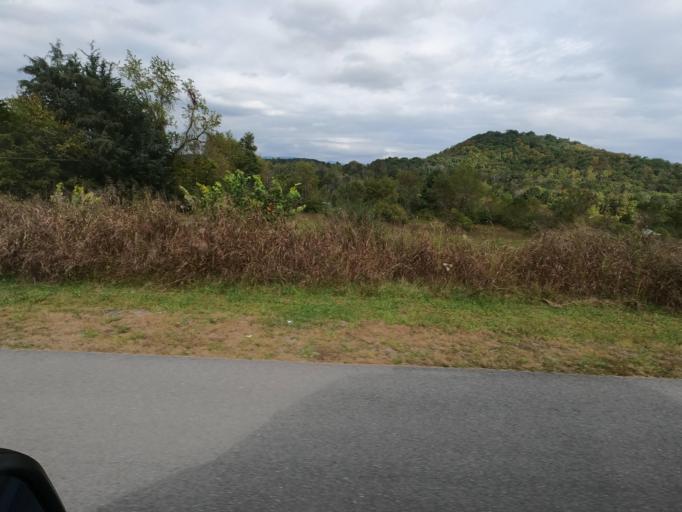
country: US
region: Tennessee
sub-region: Carter County
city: Central
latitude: 36.3209
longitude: -82.2523
